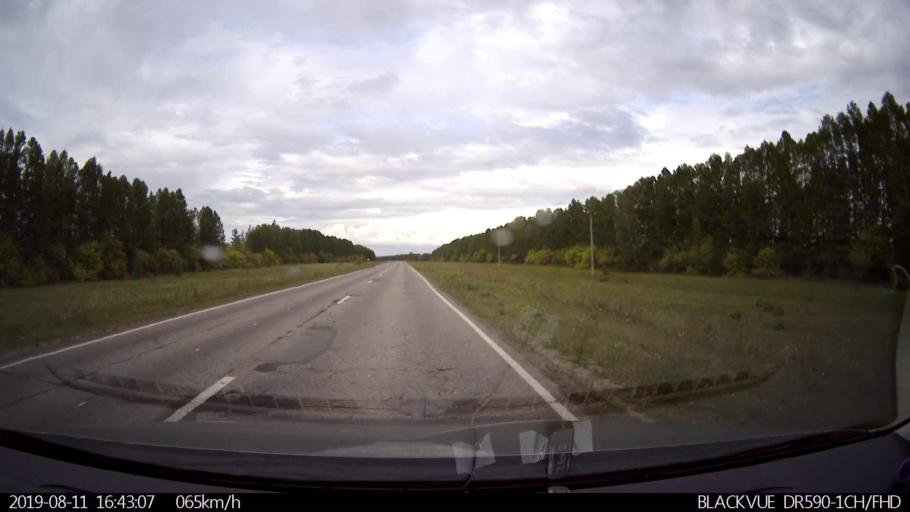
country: RU
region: Ulyanovsk
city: Mayna
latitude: 54.1660
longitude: 47.6688
